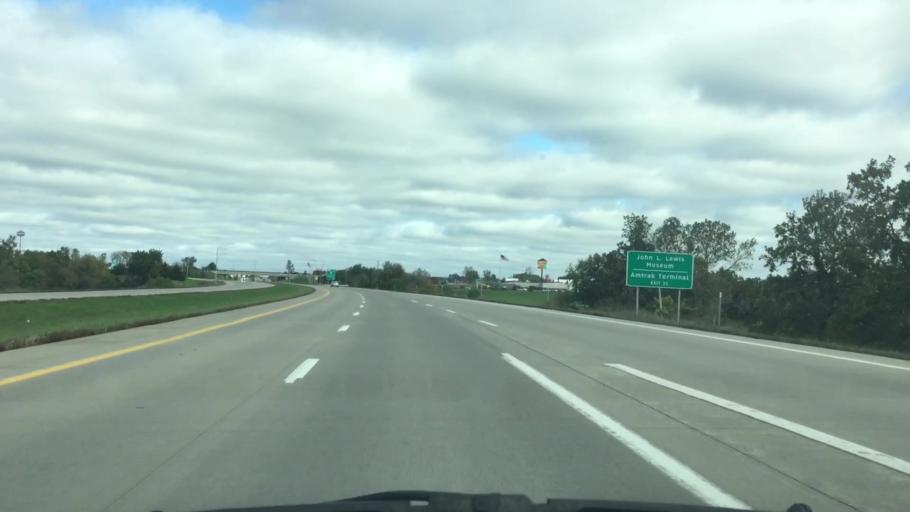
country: US
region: Iowa
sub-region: Clarke County
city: Osceola
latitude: 41.0189
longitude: -93.7936
